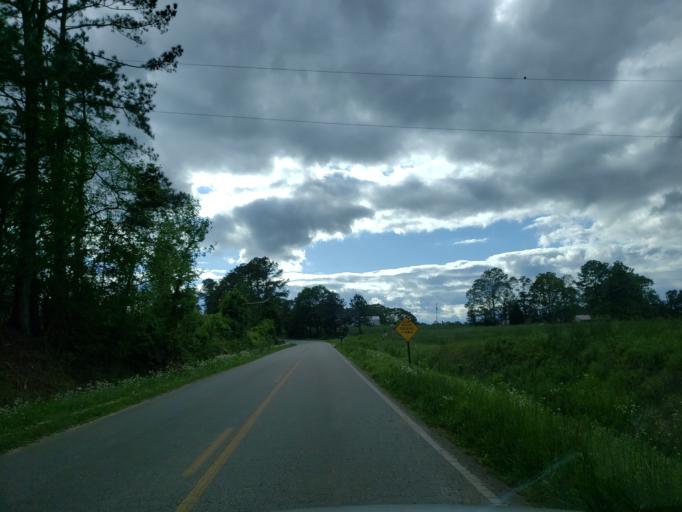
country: US
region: Georgia
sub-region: Haralson County
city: Tallapoosa
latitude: 33.7746
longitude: -85.3560
